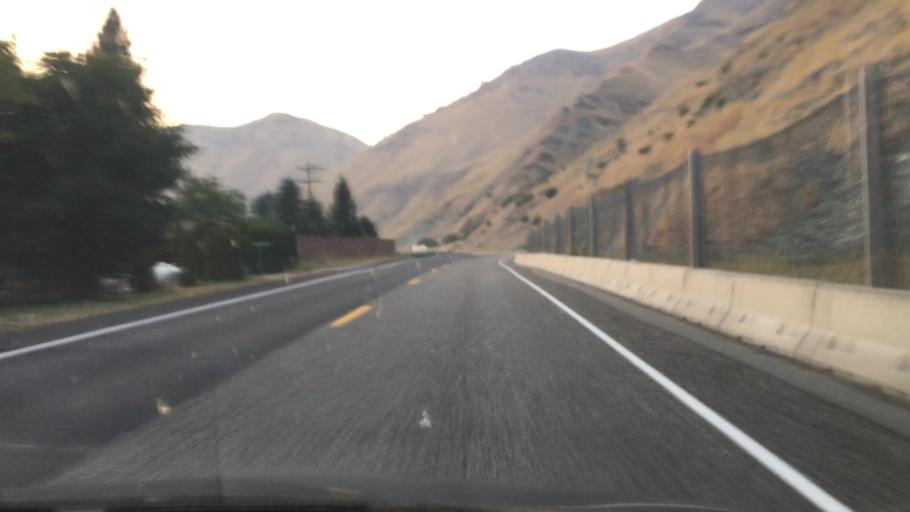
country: US
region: Idaho
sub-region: Idaho County
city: Grangeville
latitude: 45.6038
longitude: -116.2715
